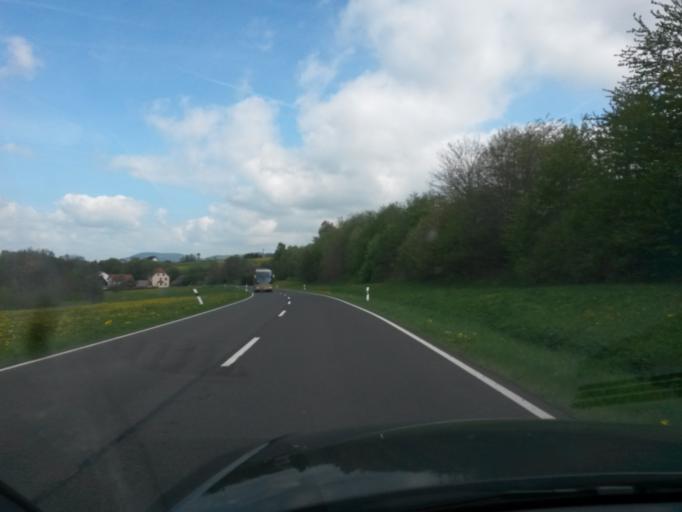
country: DE
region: Thuringia
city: Birx
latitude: 50.5189
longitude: 10.0185
